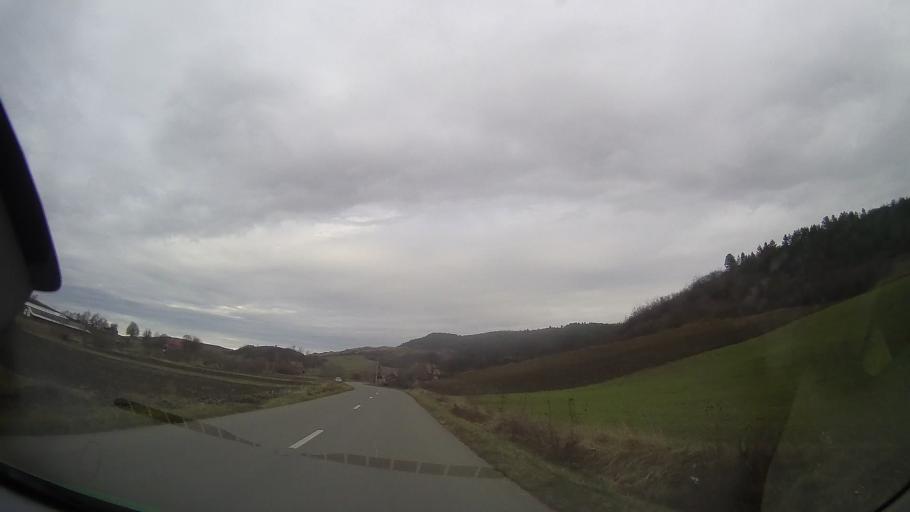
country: RO
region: Mures
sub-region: Comuna Faragau
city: Faragau
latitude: 46.7314
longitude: 24.5445
